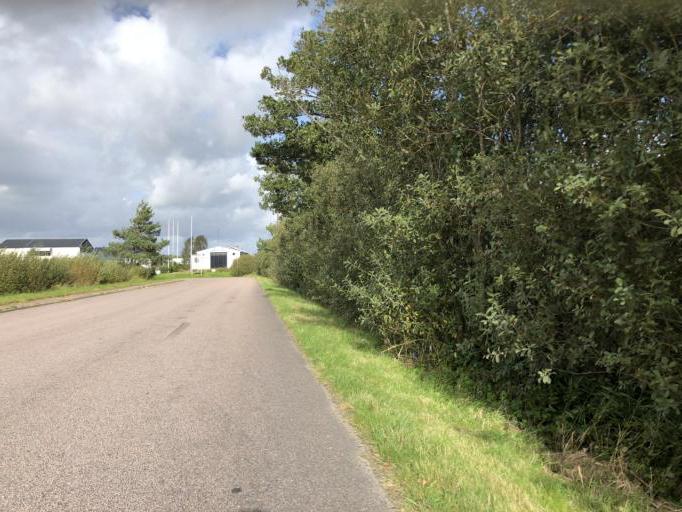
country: SE
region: Vaestra Goetaland
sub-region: Goteborg
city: Majorna
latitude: 57.7495
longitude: 11.8811
